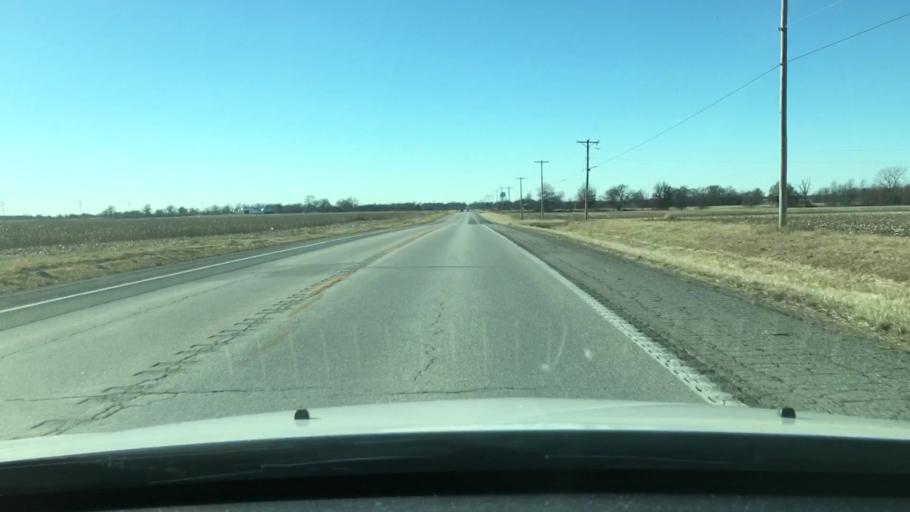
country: US
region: Missouri
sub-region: Pike County
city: Bowling Green
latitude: 39.3448
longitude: -91.3107
